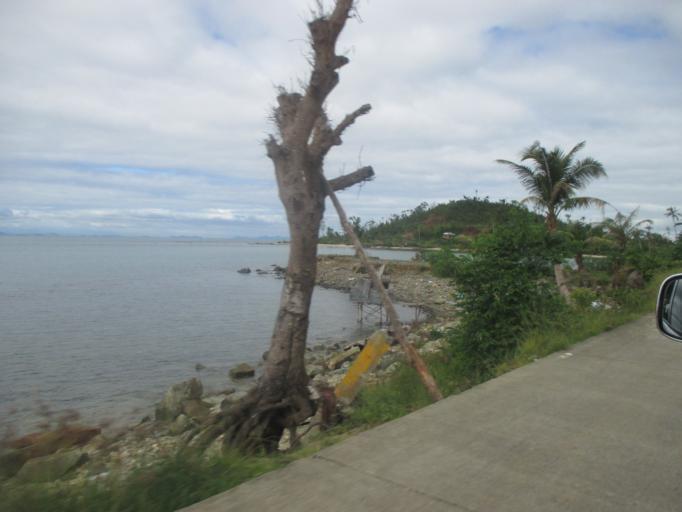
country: PH
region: Eastern Visayas
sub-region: Province of Eastern Samar
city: Lawa-an
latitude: 11.1134
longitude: 125.2103
